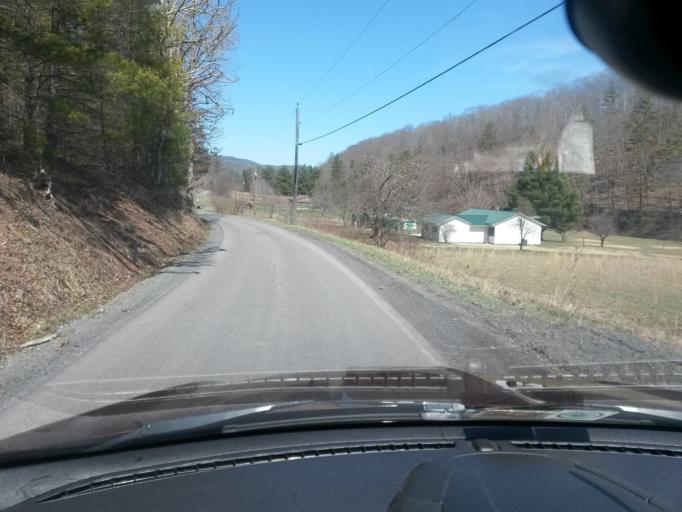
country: US
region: West Virginia
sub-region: Greenbrier County
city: White Sulphur Springs
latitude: 37.6517
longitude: -80.3255
